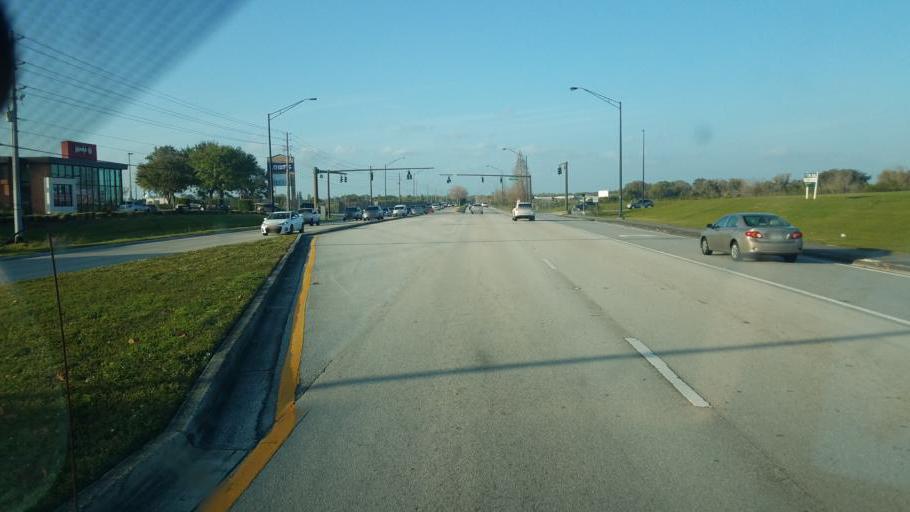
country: US
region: Florida
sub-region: Polk County
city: Crystal Lake
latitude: 27.9989
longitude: -81.9240
